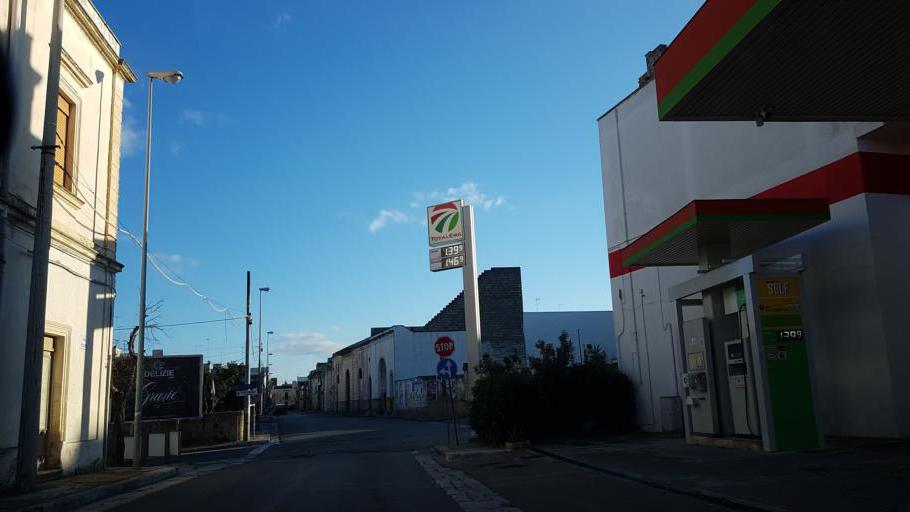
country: IT
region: Apulia
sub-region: Provincia di Lecce
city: Squinzano
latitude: 40.4380
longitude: 18.0466
